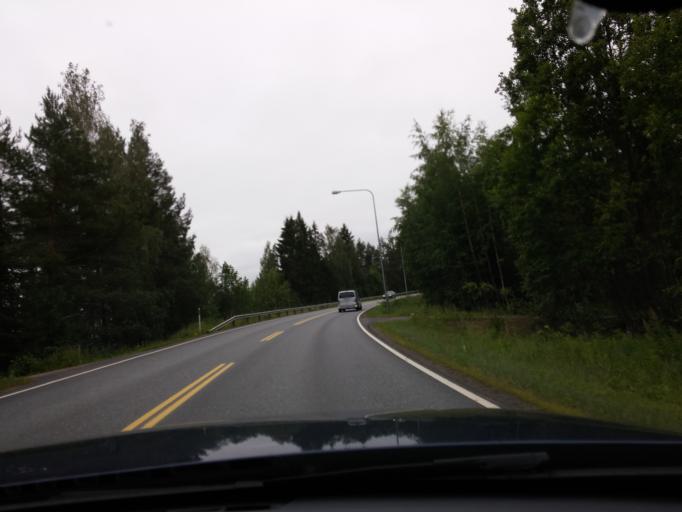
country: FI
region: Central Finland
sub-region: Jyvaeskylae
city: Korpilahti
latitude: 62.0033
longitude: 25.6796
